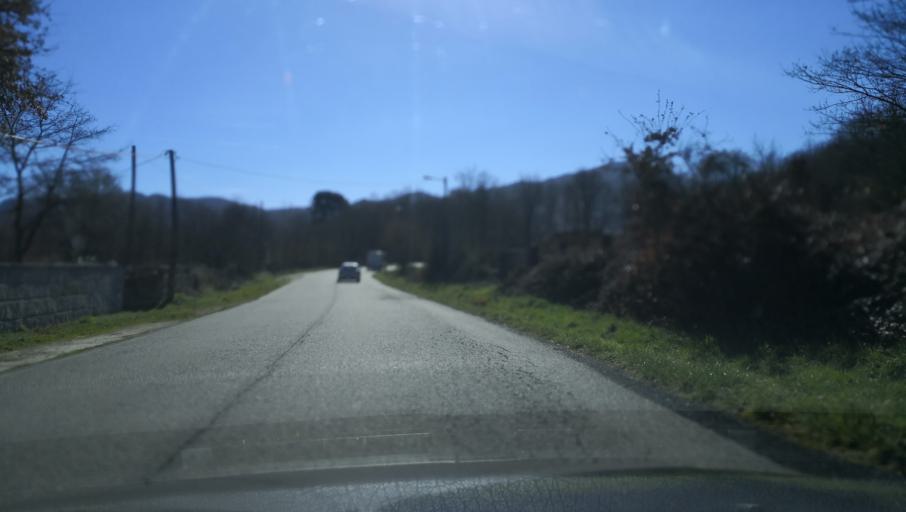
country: ES
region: Galicia
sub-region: Provincia de Ourense
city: Allariz
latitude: 42.1994
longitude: -7.8068
